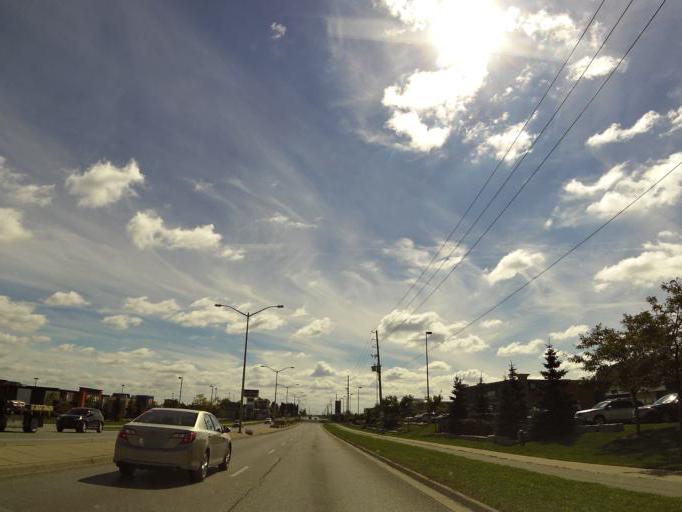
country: CA
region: Ontario
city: London
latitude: 42.9363
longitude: -81.2809
